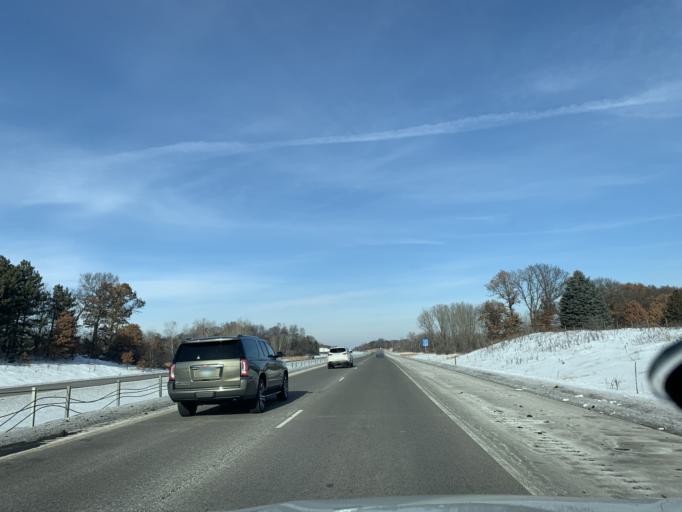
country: US
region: Minnesota
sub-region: Washington County
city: Forest Lake
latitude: 45.2982
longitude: -93.0026
